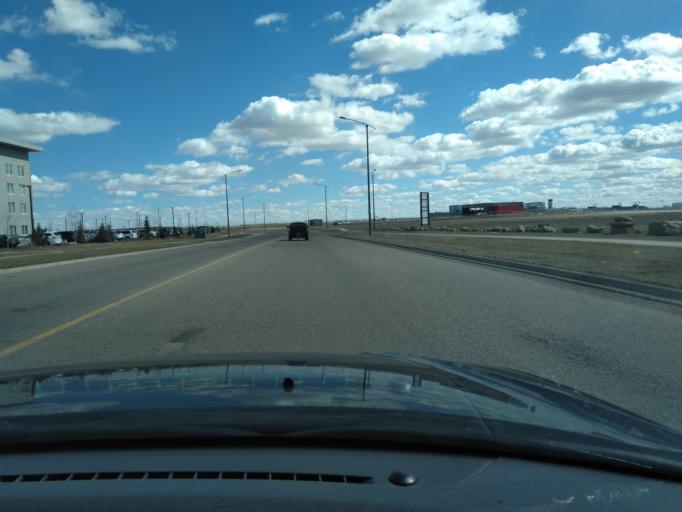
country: CA
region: Alberta
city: Calgary
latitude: 51.1365
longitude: -114.0300
